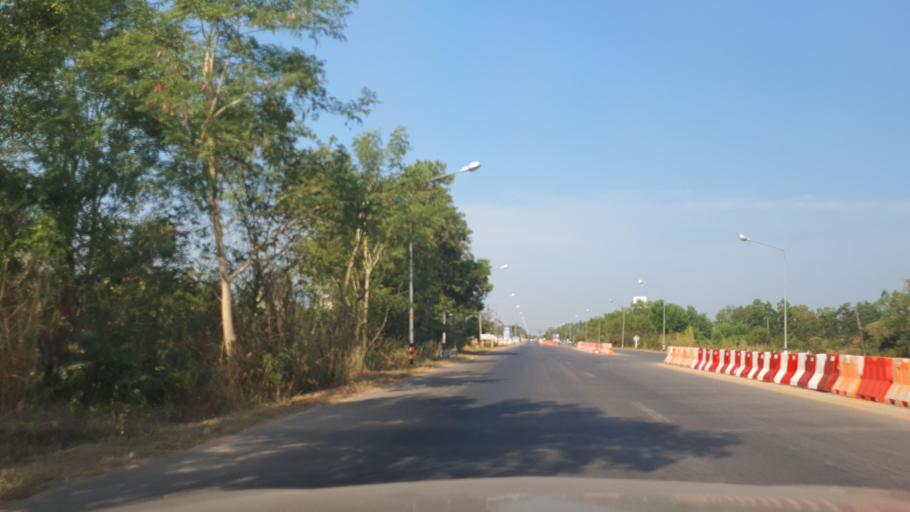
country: TH
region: Nakhon Phanom
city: Ban Phaeng
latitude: 17.9577
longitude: 104.2125
